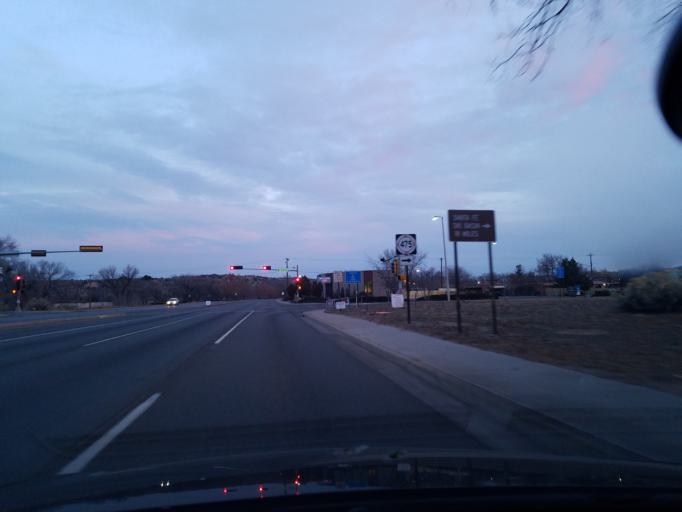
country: US
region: New Mexico
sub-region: Santa Fe County
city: Santa Fe
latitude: 35.6901
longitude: -105.9539
